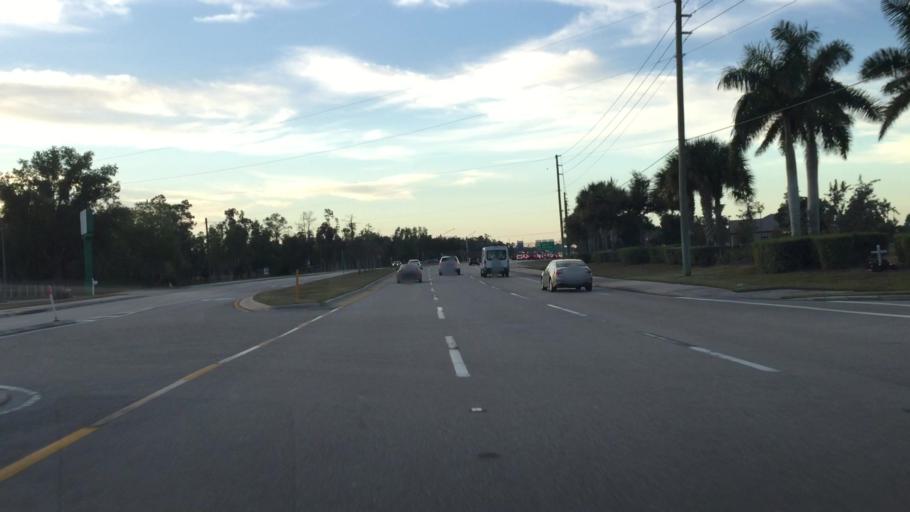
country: US
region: Florida
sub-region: Lee County
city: Gateway
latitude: 26.5509
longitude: -81.7869
